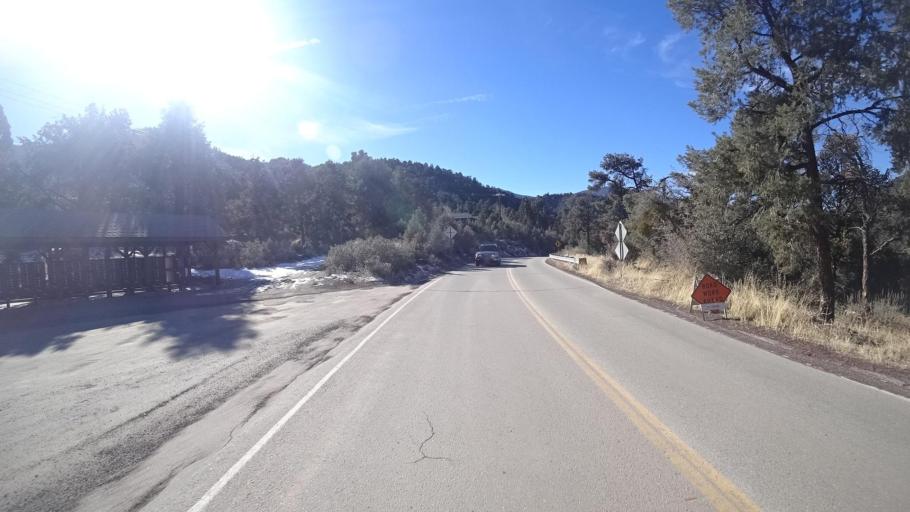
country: US
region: California
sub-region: Kern County
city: Pine Mountain Club
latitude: 34.8525
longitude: -119.1372
